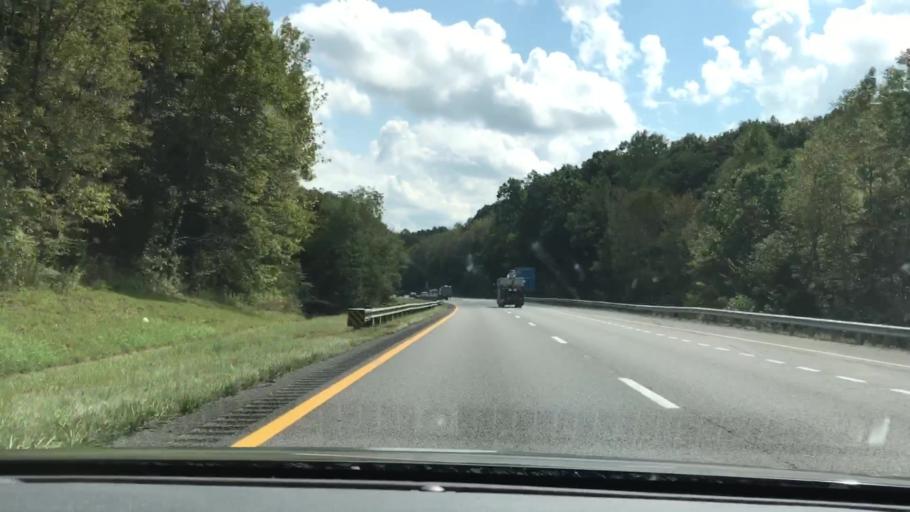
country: US
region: Tennessee
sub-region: Montgomery County
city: Clarksville
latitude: 36.5507
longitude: -87.2475
